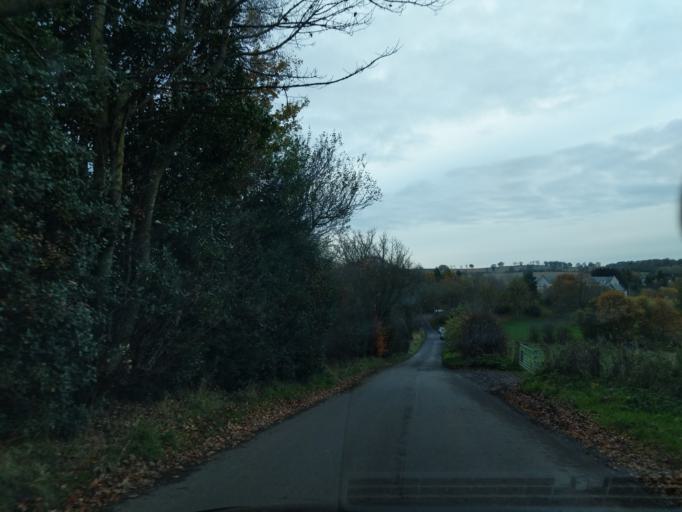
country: GB
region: Scotland
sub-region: West Lothian
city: Linlithgow
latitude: 55.9842
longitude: -3.5895
